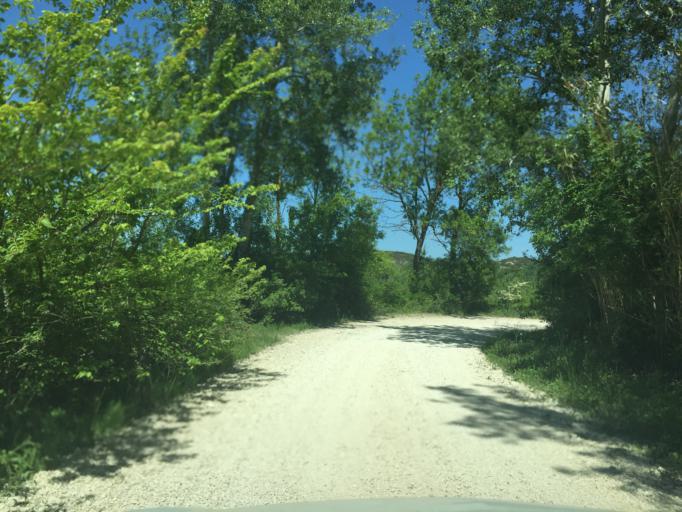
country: FR
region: Languedoc-Roussillon
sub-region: Departement du Gard
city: Roquemaure
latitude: 44.0581
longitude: 4.7945
